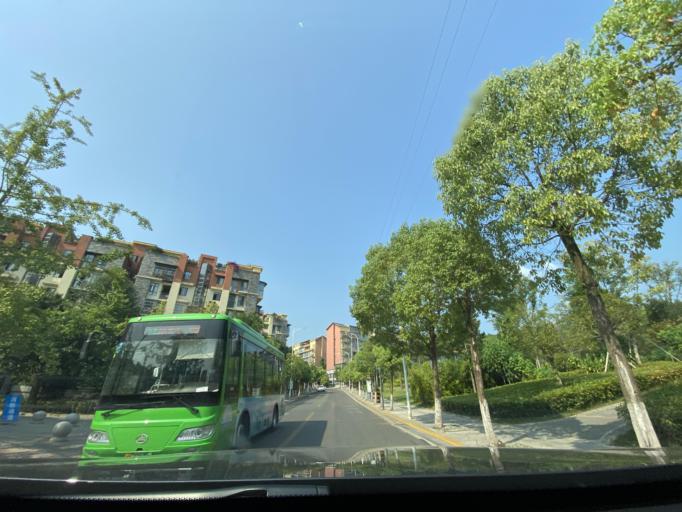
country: CN
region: Sichuan
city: Jiancheng
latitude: 30.4165
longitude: 104.5432
